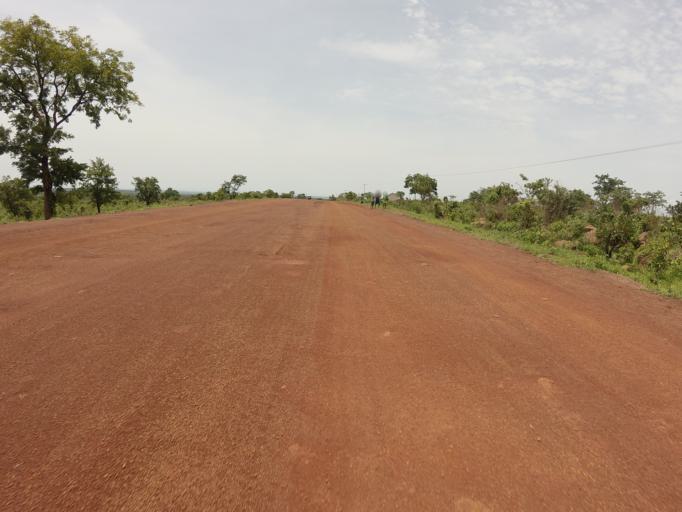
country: GH
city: Kpandae
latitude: 8.7353
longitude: 0.0904
